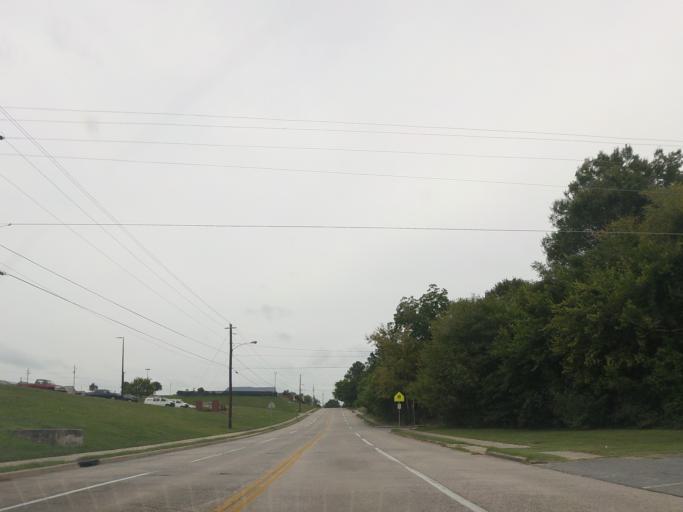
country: US
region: Georgia
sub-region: Bibb County
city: Macon
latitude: 32.8200
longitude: -83.6529
